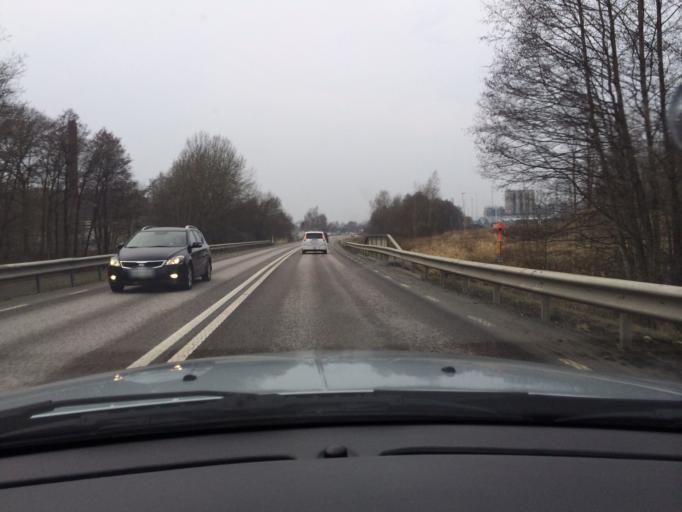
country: SE
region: Vaestra Goetaland
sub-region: Stenungsunds Kommun
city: Stenungsund
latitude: 58.0701
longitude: 11.8538
